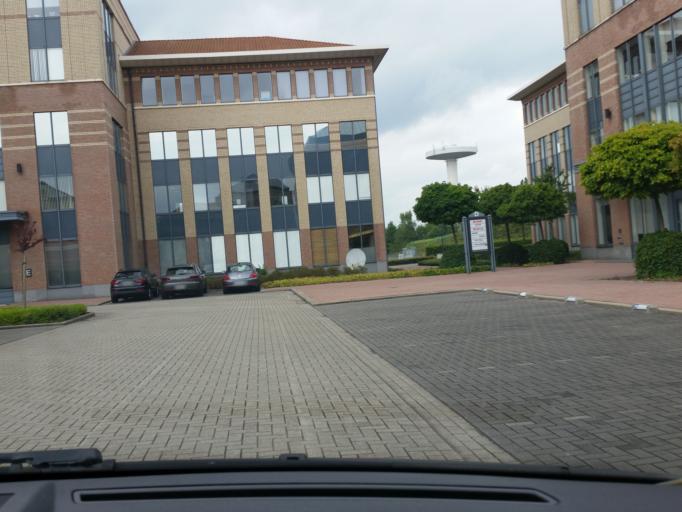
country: BE
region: Flanders
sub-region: Provincie Antwerpen
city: Mechelen
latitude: 51.0560
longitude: 4.4591
